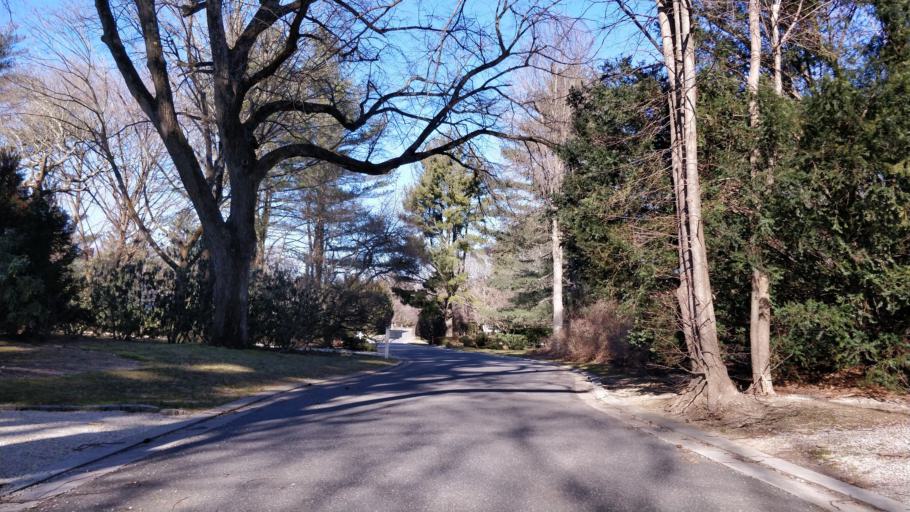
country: US
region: New York
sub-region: Nassau County
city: Old Brookville
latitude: 40.8224
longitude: -73.6101
